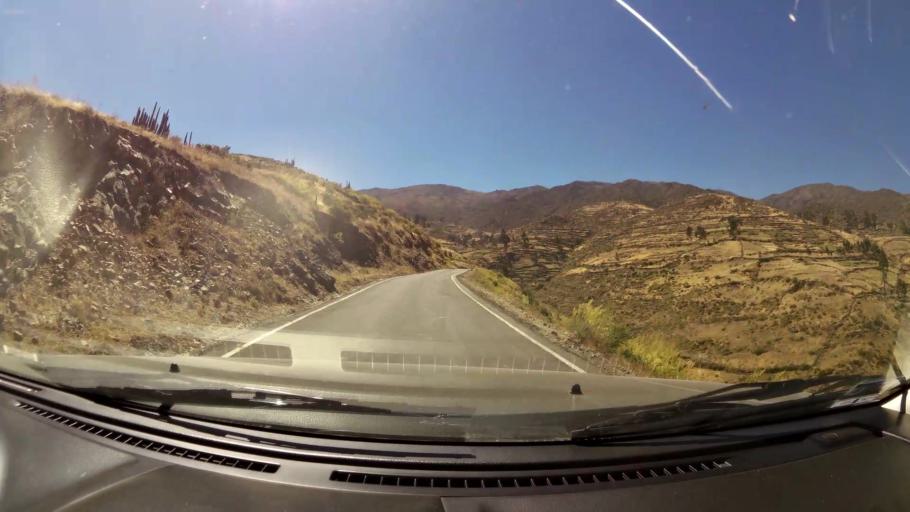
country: PE
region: Huancavelica
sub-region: Huaytara
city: Quito-Arma
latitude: -13.6850
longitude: -75.3829
